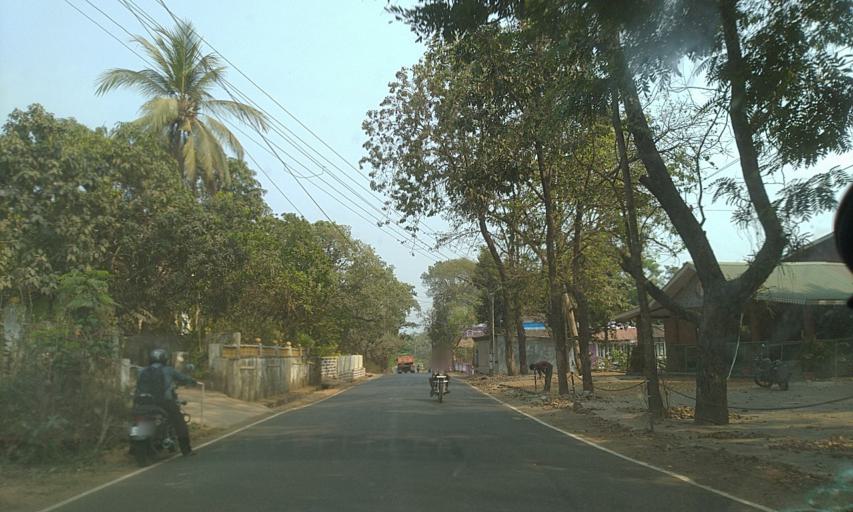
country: IN
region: Goa
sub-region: South Goa
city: Quepem
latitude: 15.2601
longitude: 74.0473
